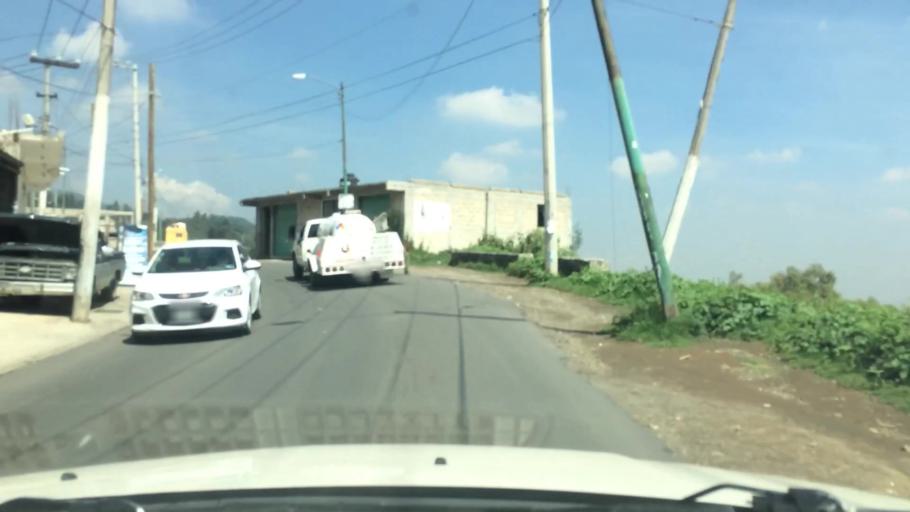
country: MX
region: Mexico City
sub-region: Tlalpan
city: Lomas de Tepemecatl
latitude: 19.2339
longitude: -99.1822
